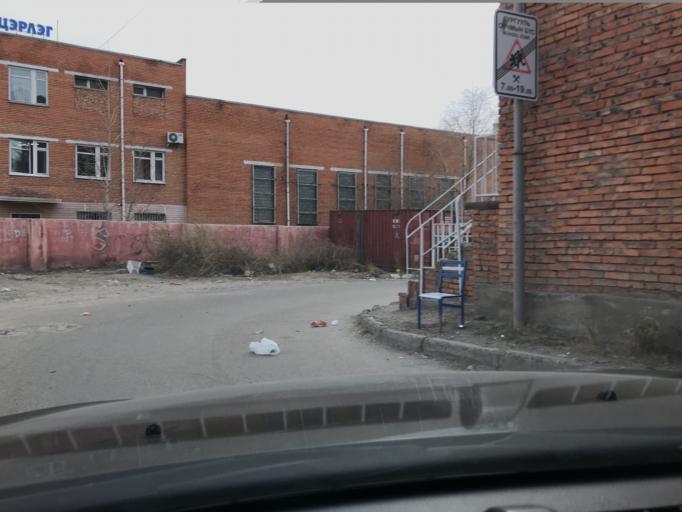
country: MN
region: Ulaanbaatar
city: Ulaanbaatar
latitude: 47.9184
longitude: 106.9559
